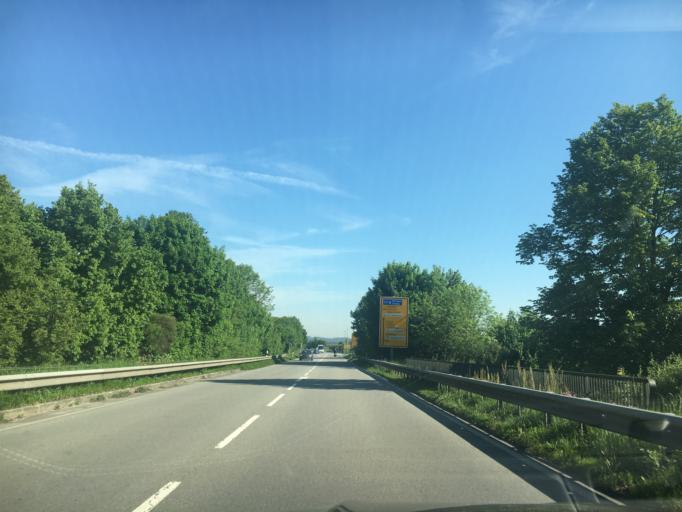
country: DE
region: Bavaria
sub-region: Upper Bavaria
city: Altoetting
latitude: 48.2245
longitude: 12.6574
